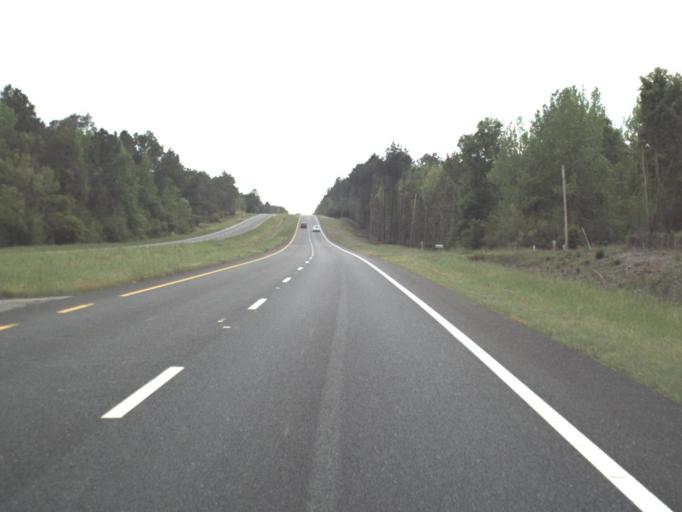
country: US
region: Florida
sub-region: Escambia County
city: Molino
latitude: 30.8246
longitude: -87.3339
